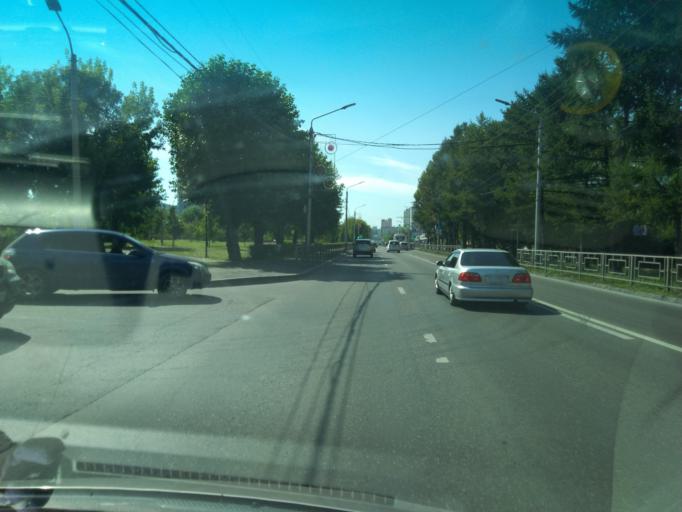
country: RU
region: Krasnoyarskiy
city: Krasnoyarsk
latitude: 56.0125
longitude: 92.8186
